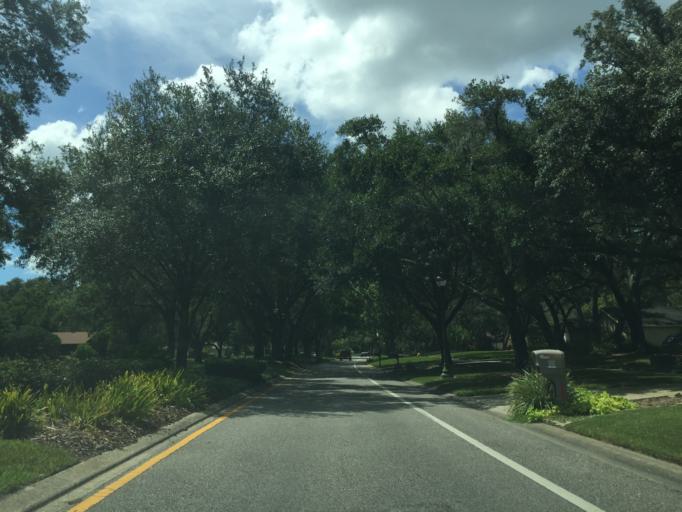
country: US
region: Florida
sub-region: Seminole County
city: Winter Springs
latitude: 28.6743
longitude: -81.2639
